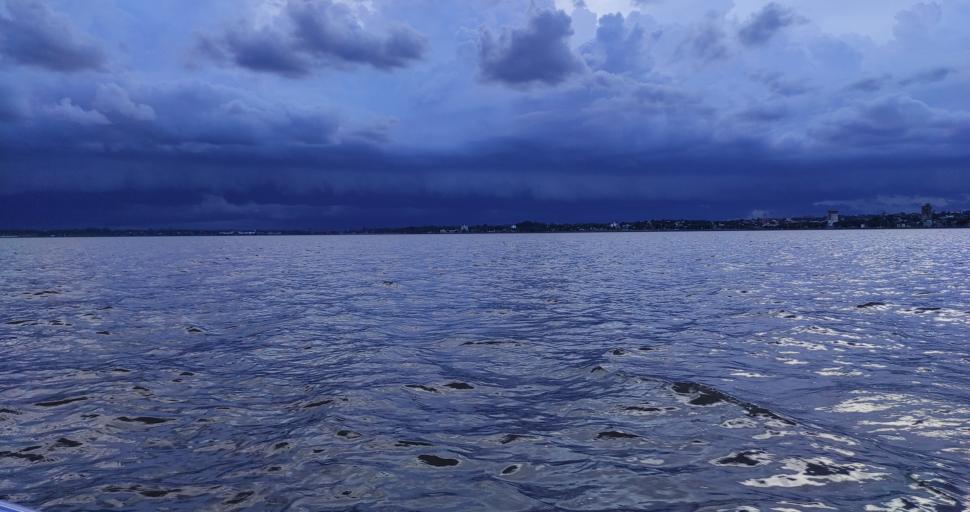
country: AR
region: Misiones
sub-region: Departamento de Capital
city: Posadas
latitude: -27.3893
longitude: -55.8751
